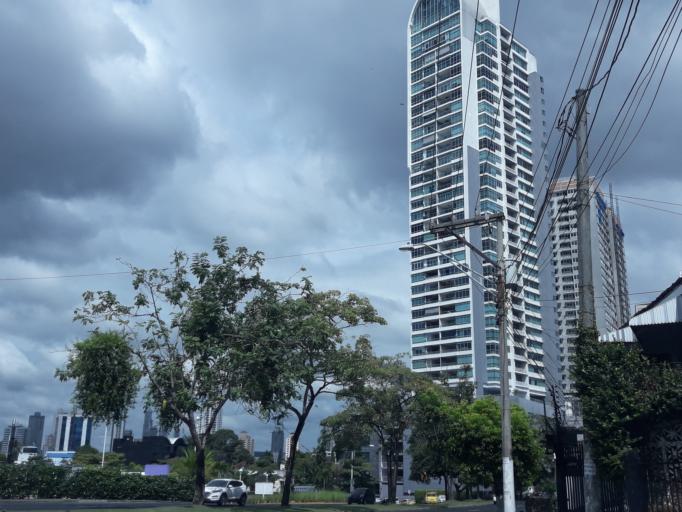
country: PA
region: Panama
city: Panama
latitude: 8.9871
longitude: -79.5100
